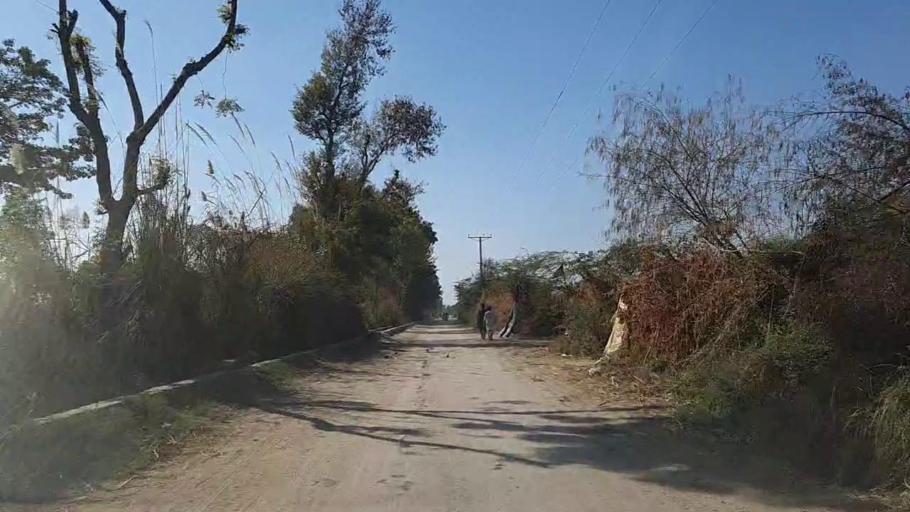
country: PK
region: Sindh
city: Nawabshah
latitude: 26.2443
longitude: 68.4310
